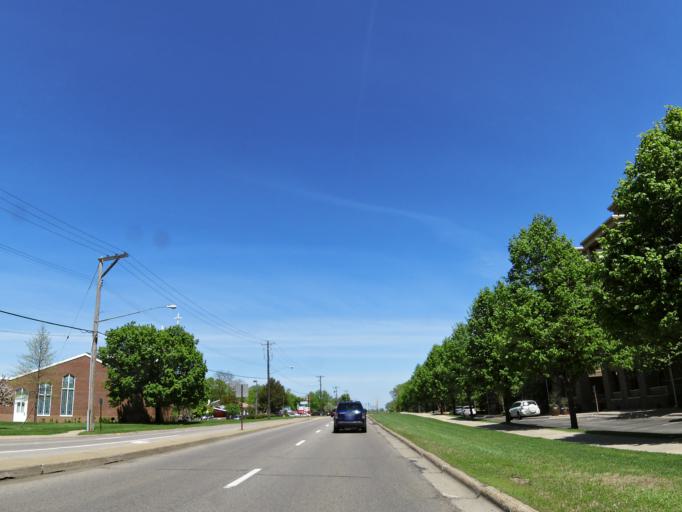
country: US
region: Minnesota
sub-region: Hennepin County
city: Bloomington
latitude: 44.8188
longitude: -93.3084
